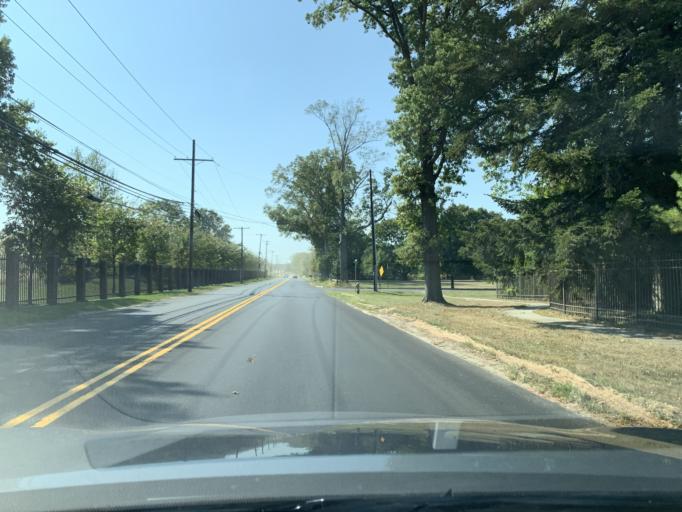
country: US
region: New Jersey
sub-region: Monmouth County
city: Tinton Falls
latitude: 40.3021
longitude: -74.0832
